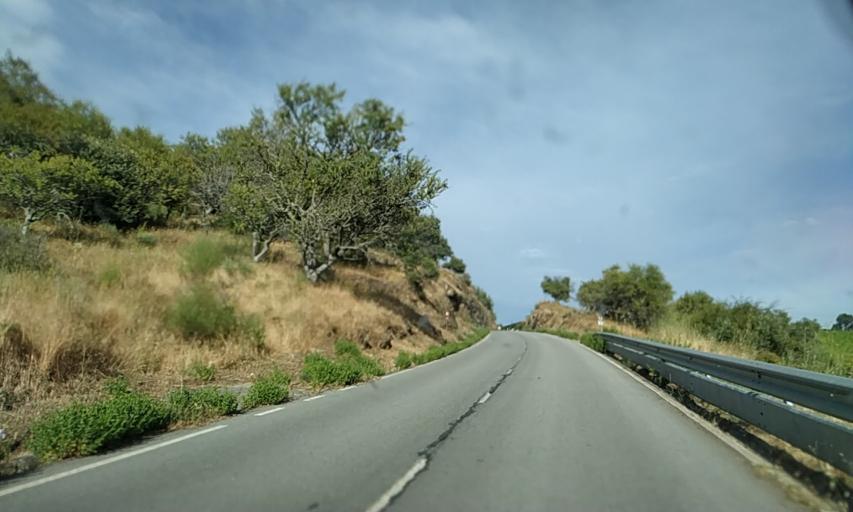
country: PT
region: Viseu
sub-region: Sao Joao da Pesqueira
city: Sao Joao da Pesqueira
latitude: 41.1426
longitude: -7.4286
